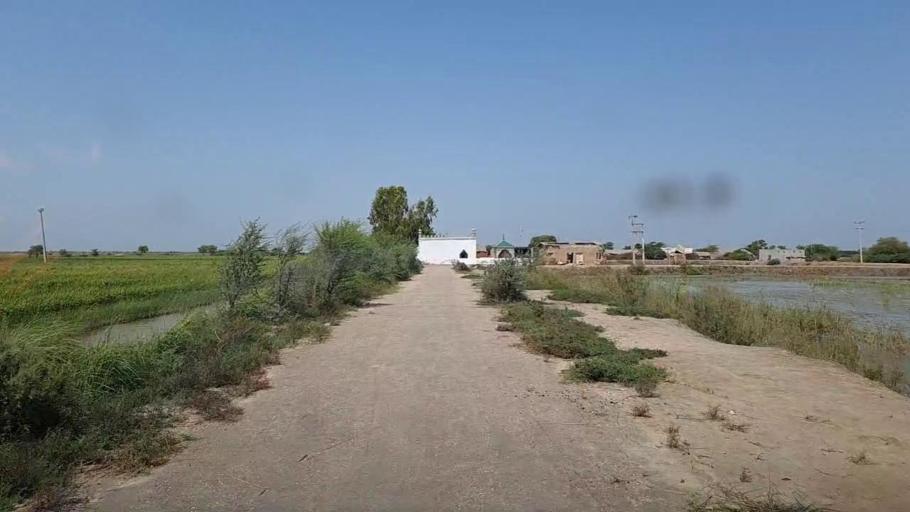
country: PK
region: Sindh
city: Mirpur Batoro
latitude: 24.6438
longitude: 68.4513
